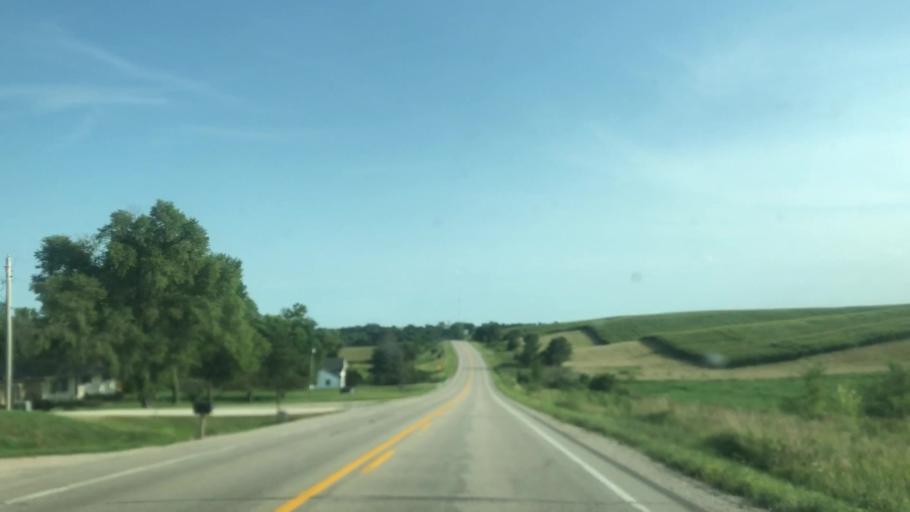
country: US
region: Iowa
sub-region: Marshall County
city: Marshalltown
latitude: 42.0394
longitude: -93.0001
